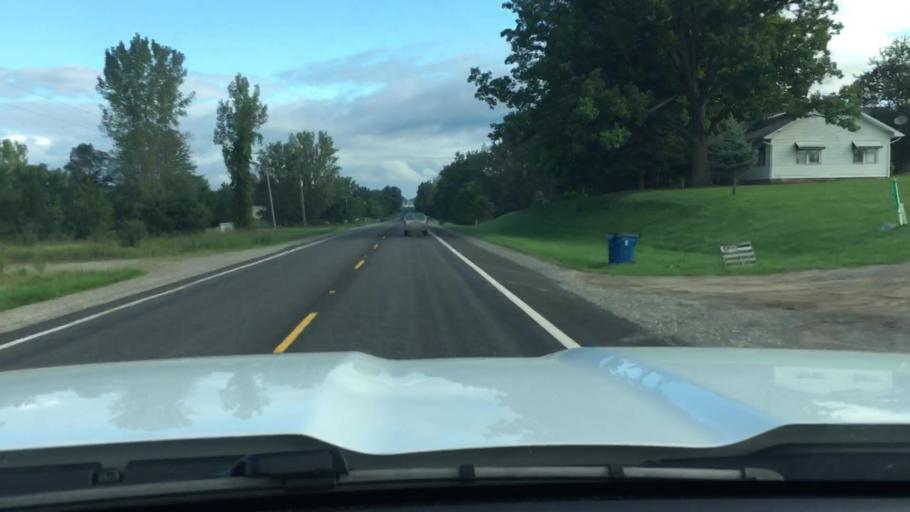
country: US
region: Michigan
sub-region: Tuscola County
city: Caro
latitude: 43.3547
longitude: -83.3827
